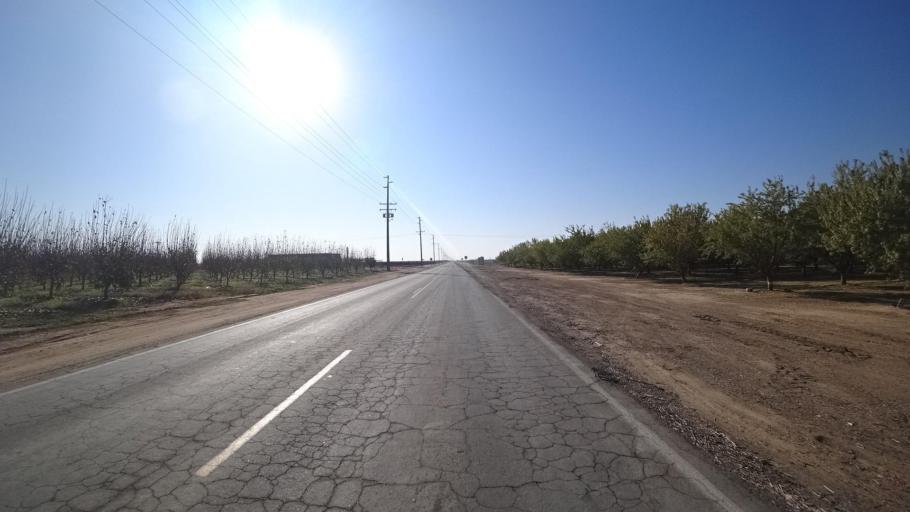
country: US
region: California
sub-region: Kern County
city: Delano
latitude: 35.7481
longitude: -119.2233
